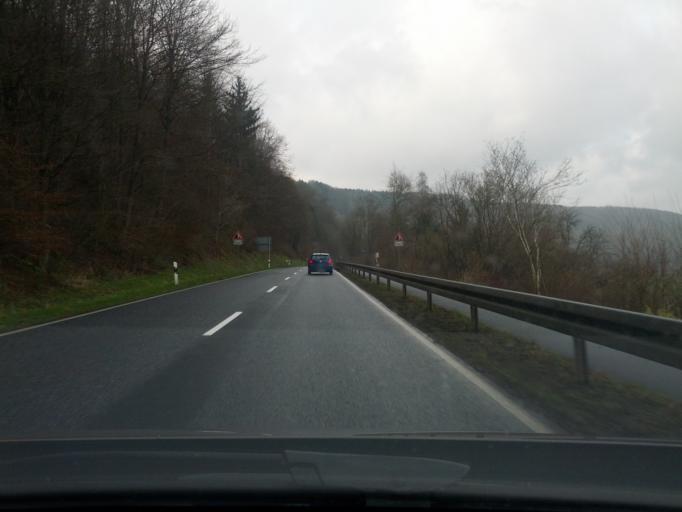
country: DE
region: Lower Saxony
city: Bad Karlshafen
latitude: 51.6283
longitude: 9.4991
